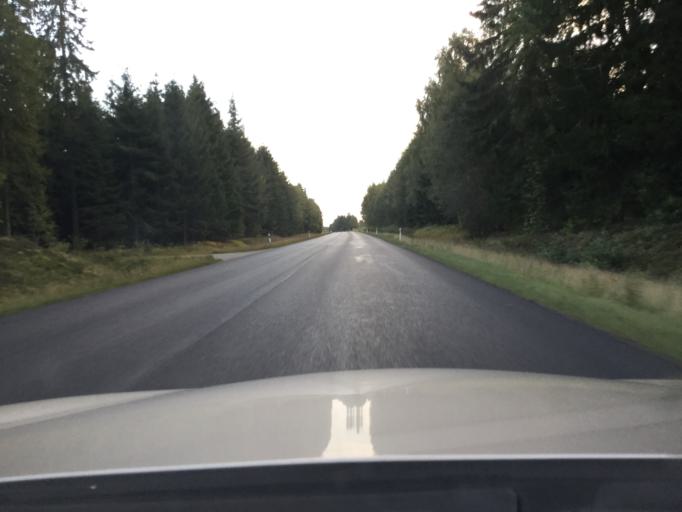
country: SE
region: Kronoberg
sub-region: Almhults Kommun
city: AElmhult
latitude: 56.6036
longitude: 14.2199
